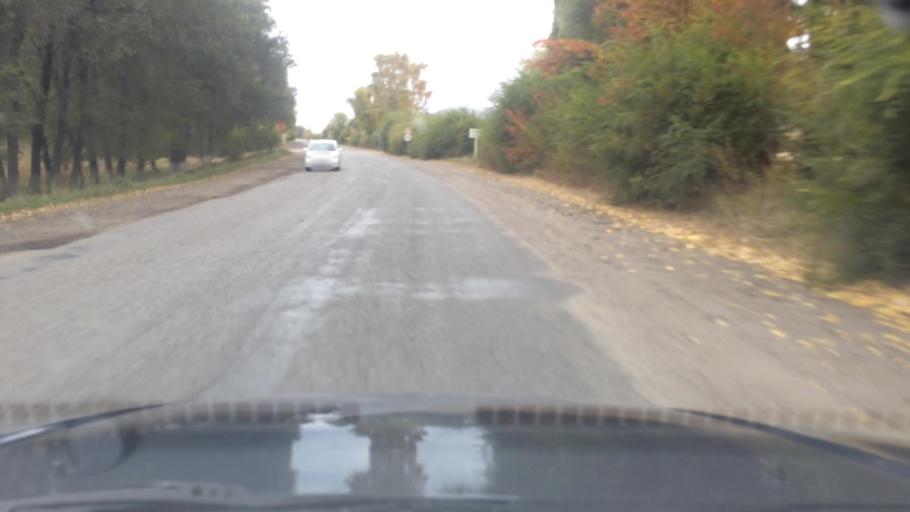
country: KG
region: Ysyk-Koel
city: Tyup
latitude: 42.7808
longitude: 78.2199
